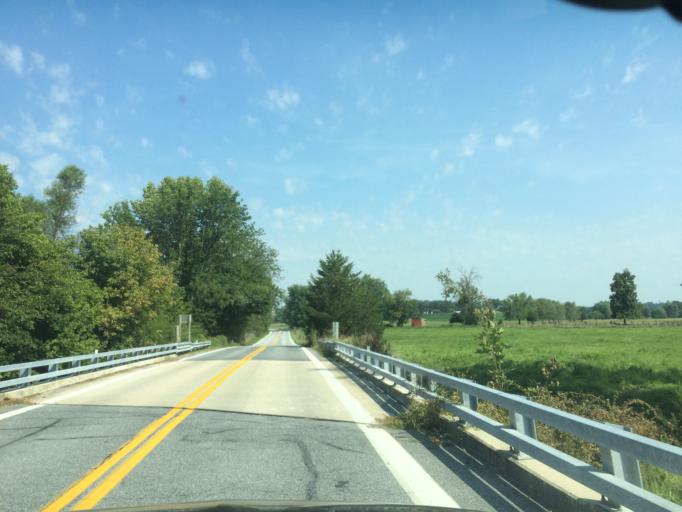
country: US
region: Maryland
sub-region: Carroll County
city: New Windsor
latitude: 39.6086
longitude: -77.1137
